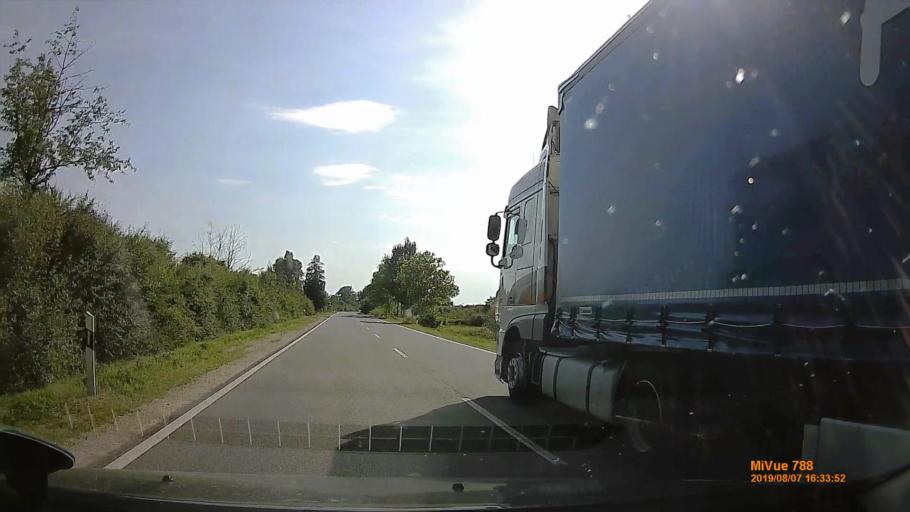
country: HU
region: Zala
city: Lenti
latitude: 46.6287
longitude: 16.4720
